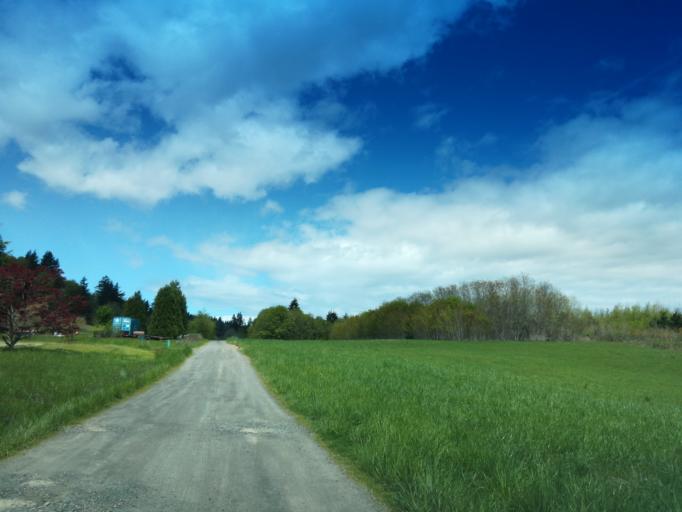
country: US
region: Oregon
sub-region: Clackamas County
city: Damascus
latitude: 45.4511
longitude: -122.4480
